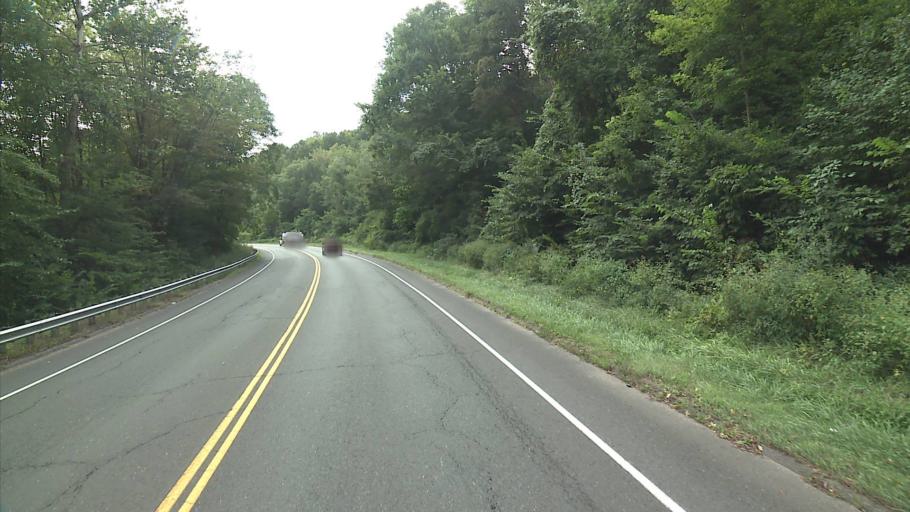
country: US
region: Connecticut
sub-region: Hartford County
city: Tariffville
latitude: 41.9033
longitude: -72.7613
